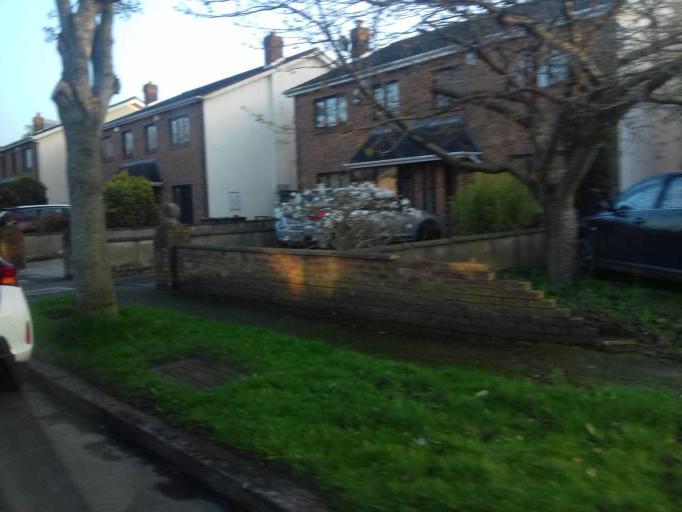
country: IE
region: Leinster
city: Hartstown
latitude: 53.3866
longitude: -6.4244
